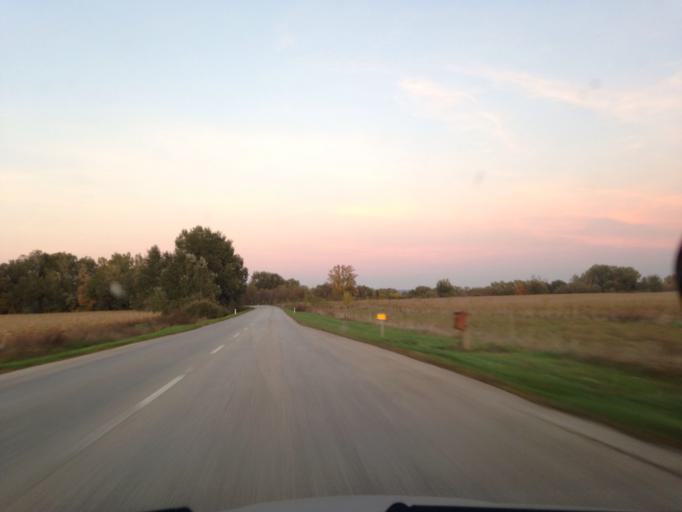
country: SK
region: Nitriansky
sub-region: Okres Komarno
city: Hurbanovo
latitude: 47.8061
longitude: 18.1981
